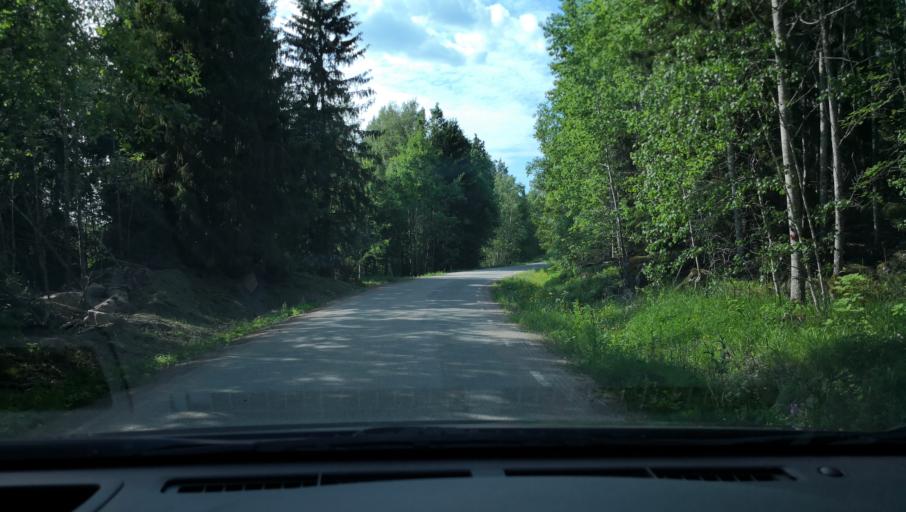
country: SE
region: Uppsala
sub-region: Enkopings Kommun
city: Orsundsbro
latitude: 59.8398
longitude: 17.2040
